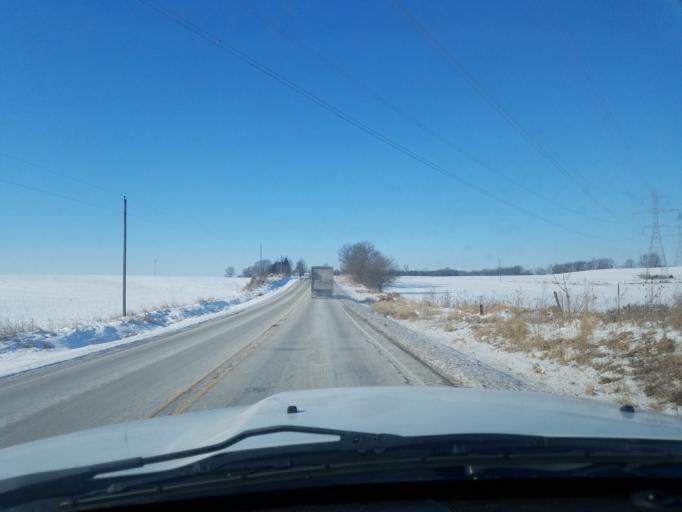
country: US
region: Indiana
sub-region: Noble County
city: Avilla
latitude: 41.3947
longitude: -85.2765
